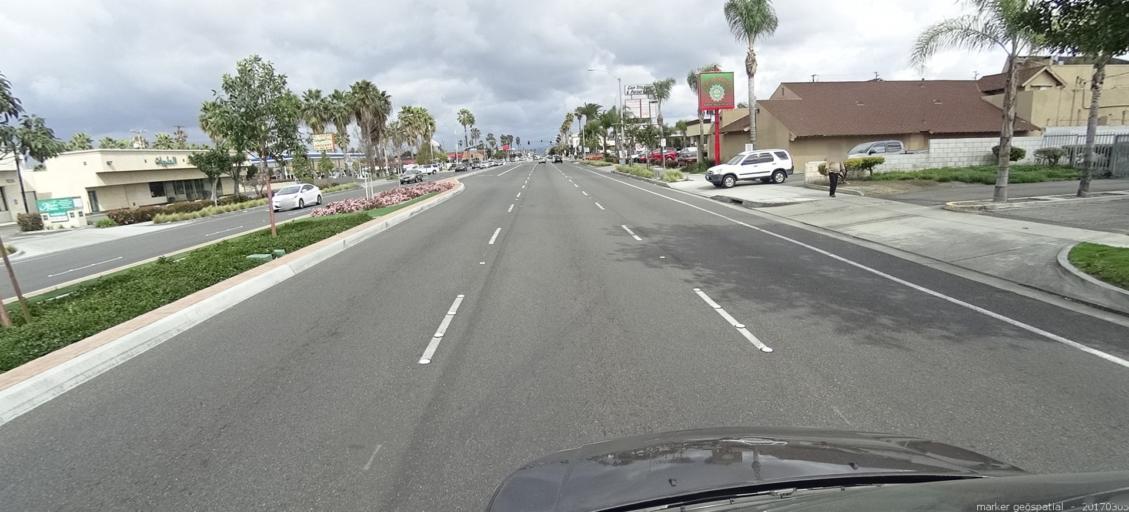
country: US
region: California
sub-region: Orange County
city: Stanton
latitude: 33.8162
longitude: -117.9589
